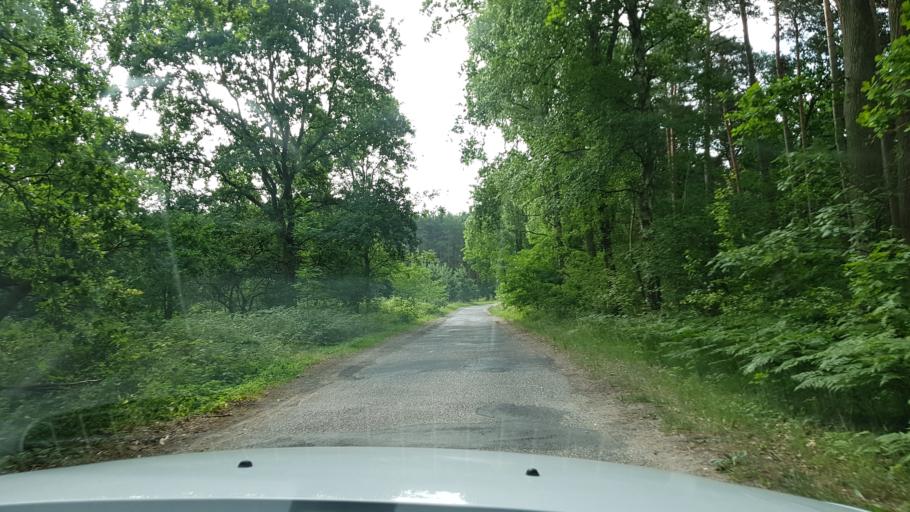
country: PL
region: West Pomeranian Voivodeship
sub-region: Powiat gryfinski
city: Gryfino
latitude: 53.2476
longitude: 14.5617
